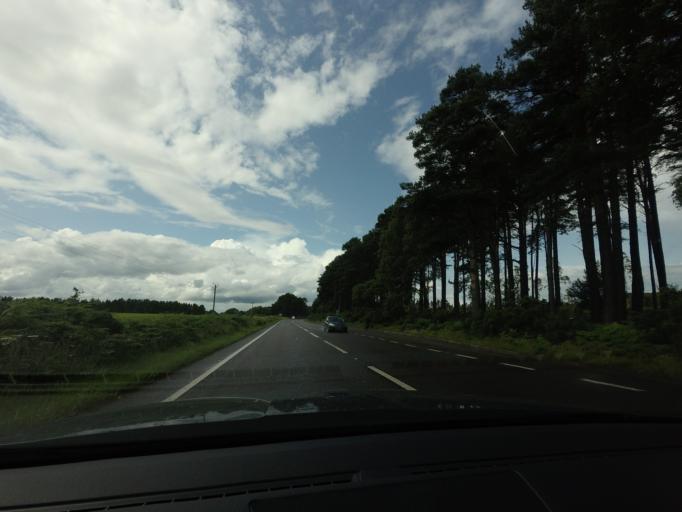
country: GB
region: Scotland
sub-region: Moray
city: Lhanbryd
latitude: 57.6320
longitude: -3.1815
